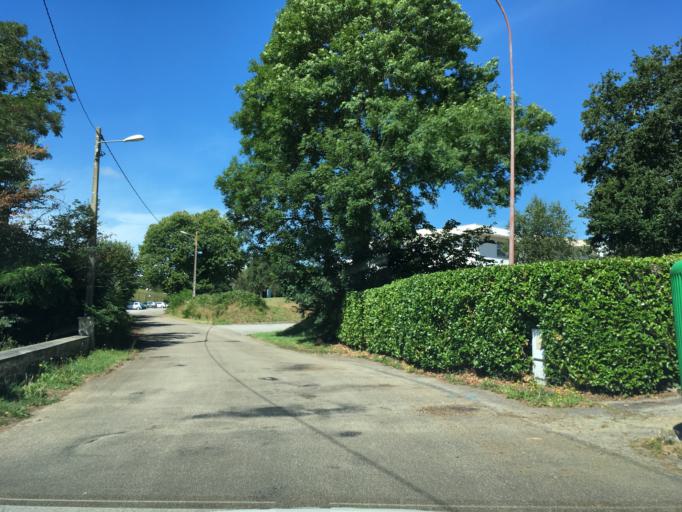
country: FR
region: Brittany
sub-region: Departement du Finistere
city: Quimper
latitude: 48.0004
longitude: -4.0784
